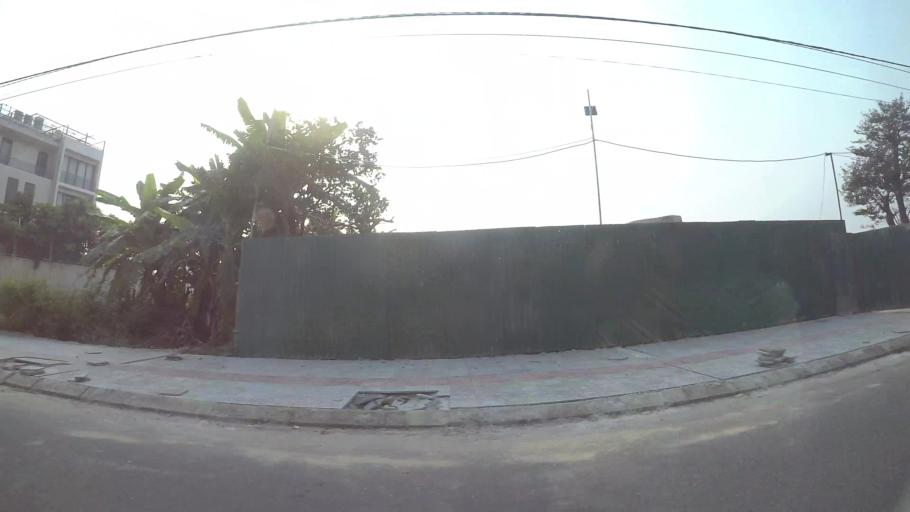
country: VN
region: Da Nang
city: Cam Le
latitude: 16.0153
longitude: 108.2172
